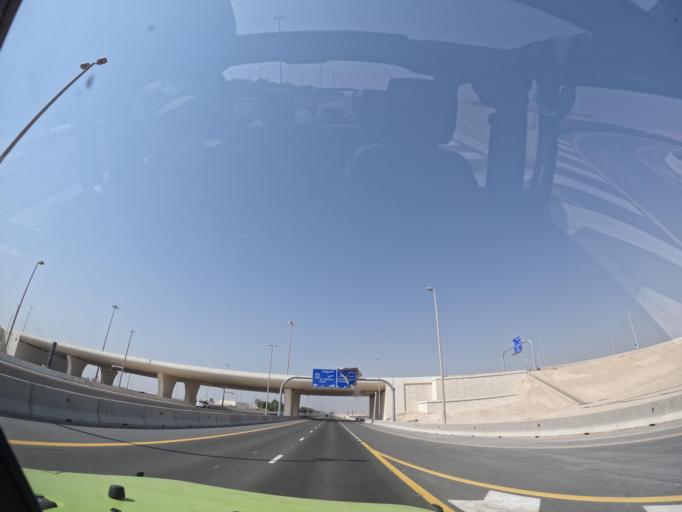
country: AE
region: Abu Dhabi
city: Abu Dhabi
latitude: 24.4297
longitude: 54.6783
